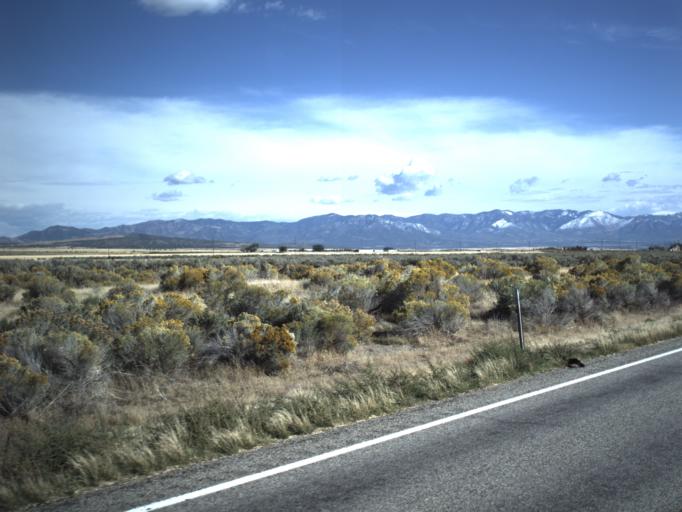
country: US
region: Utah
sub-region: Millard County
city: Delta
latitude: 39.2257
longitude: -112.4239
